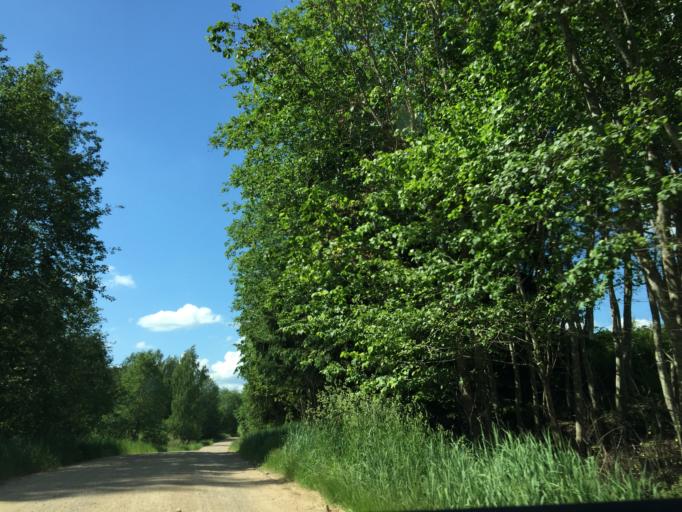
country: LV
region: Priekuli
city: Priekuli
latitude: 57.2539
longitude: 25.3932
